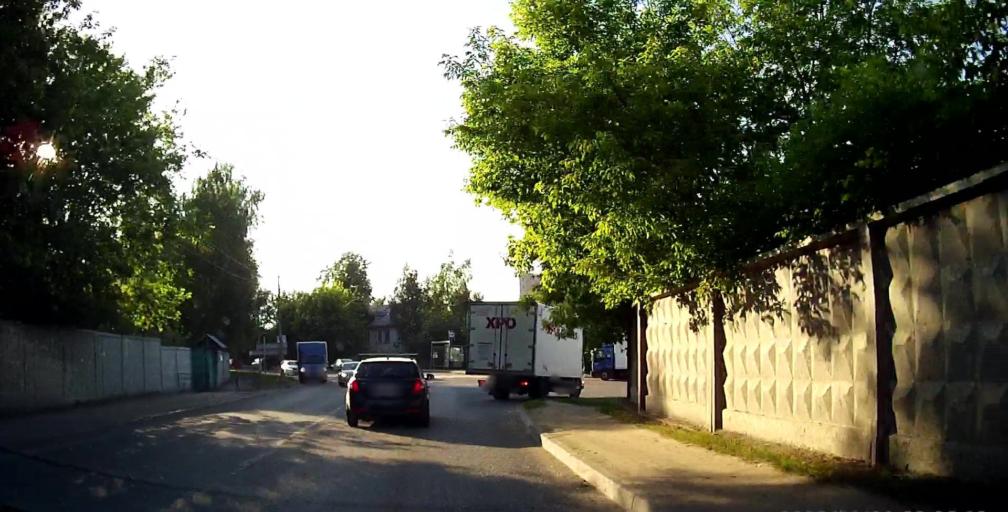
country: RU
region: Moskovskaya
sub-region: Podol'skiy Rayon
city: Podol'sk
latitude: 55.4384
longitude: 37.5824
